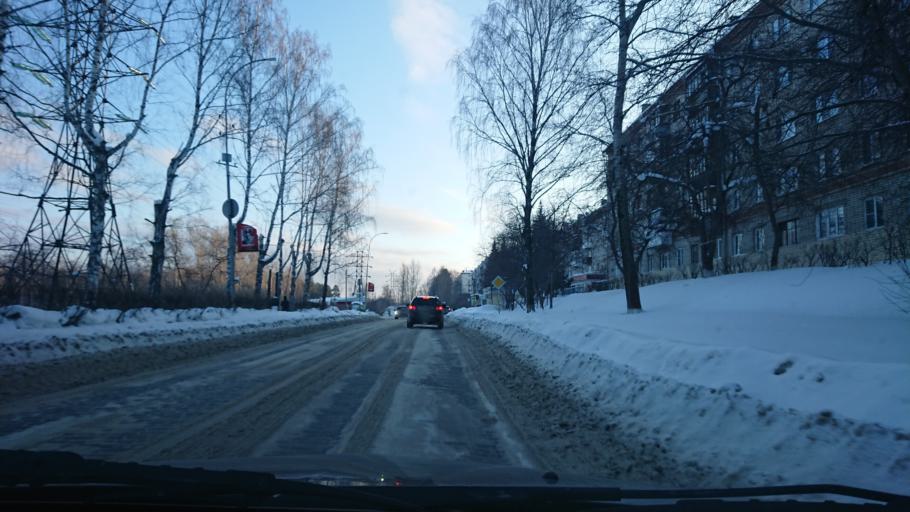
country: RU
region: Sverdlovsk
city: Degtyarsk
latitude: 56.6938
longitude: 60.0891
